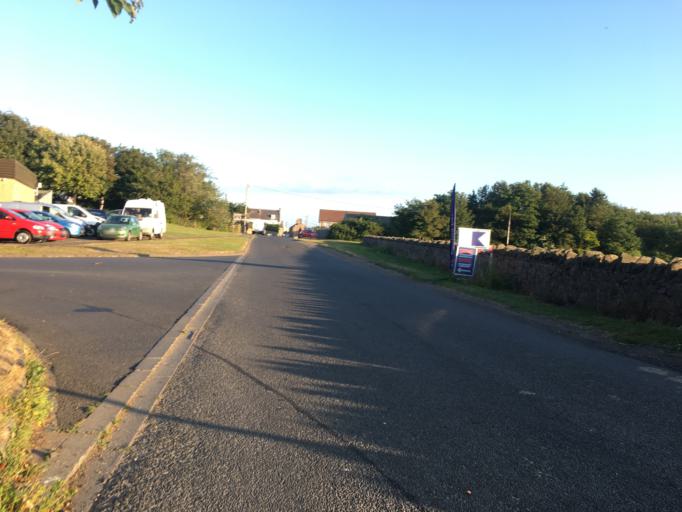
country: GB
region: England
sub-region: Northumberland
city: North Sunderland
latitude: 55.5786
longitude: -1.6681
